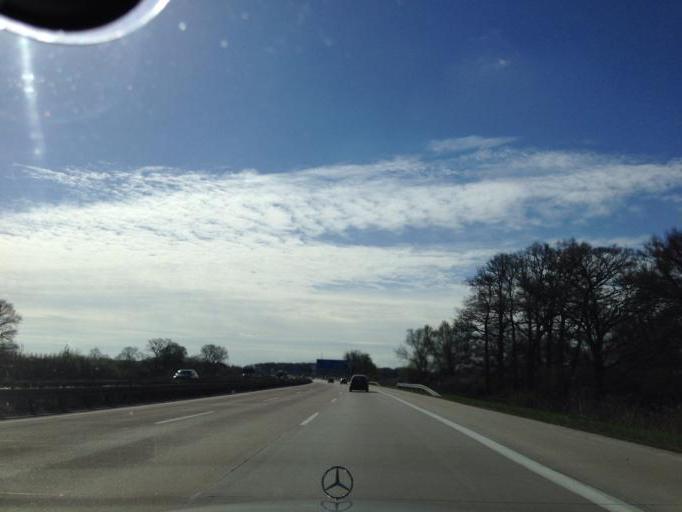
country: DE
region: Lower Saxony
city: Isernhagen Farster Bauerschaft
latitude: 52.4502
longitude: 9.8625
